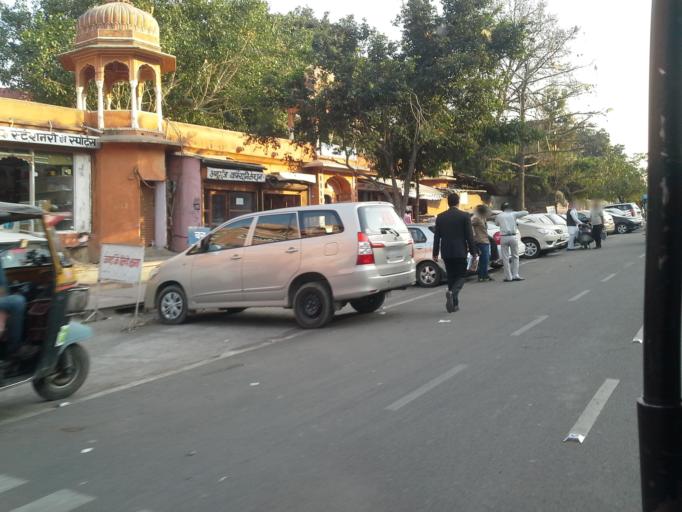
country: IN
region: Rajasthan
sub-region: Jaipur
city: Jaipur
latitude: 26.9180
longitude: 75.8211
